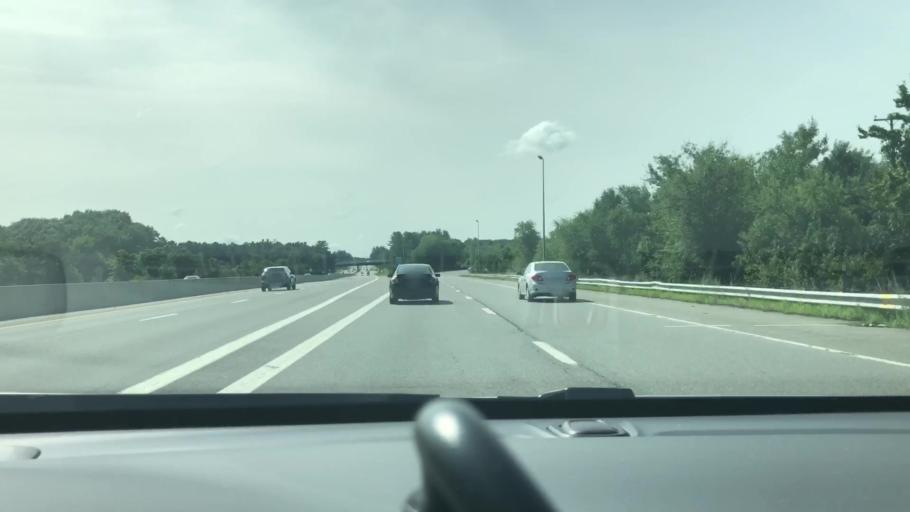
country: US
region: New Hampshire
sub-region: Hillsborough County
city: Bedford
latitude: 42.9562
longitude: -71.4746
